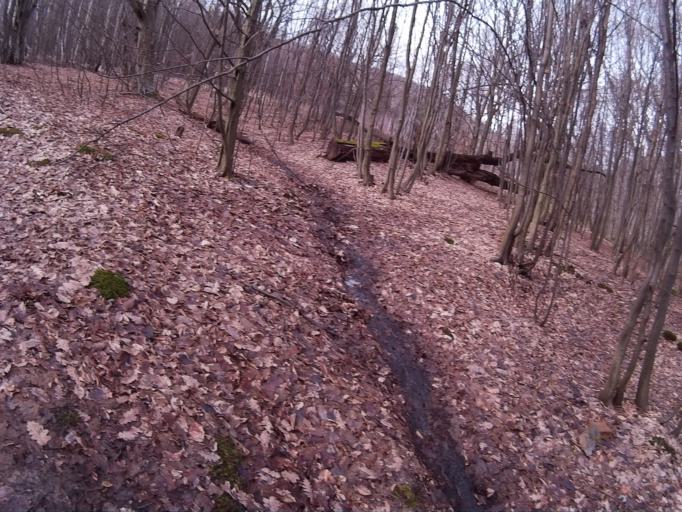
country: HU
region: Borsod-Abauj-Zemplen
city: Gonc
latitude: 48.4086
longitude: 21.4009
